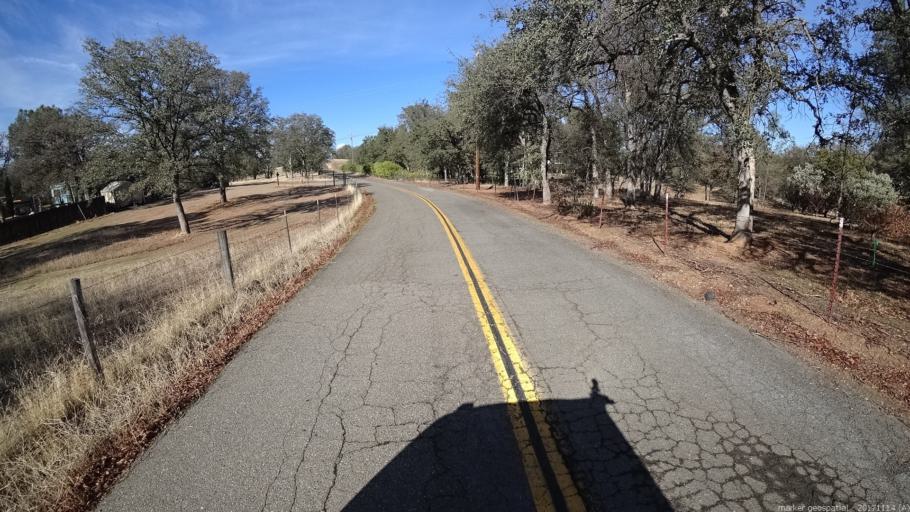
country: US
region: California
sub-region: Shasta County
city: Anderson
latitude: 40.4037
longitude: -122.4085
